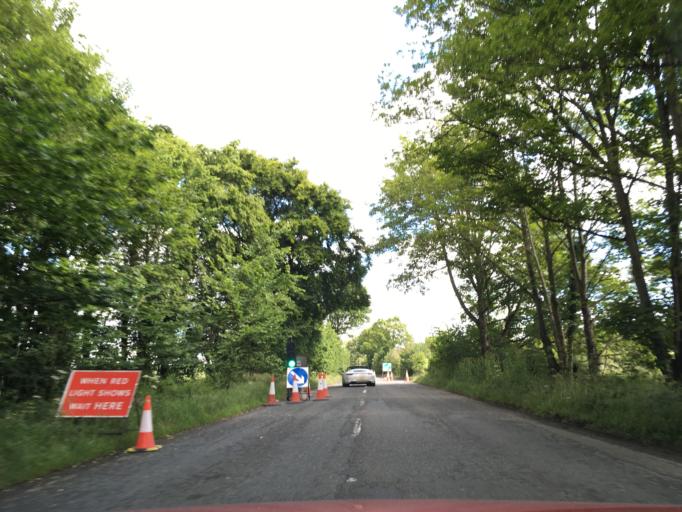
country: GB
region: England
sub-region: Oxfordshire
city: Burford
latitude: 51.7621
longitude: -1.6527
